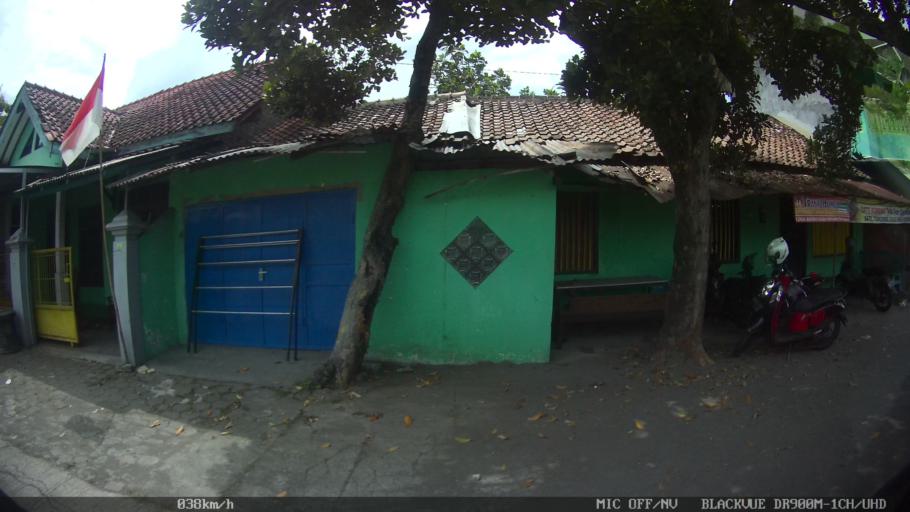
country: ID
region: Daerah Istimewa Yogyakarta
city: Depok
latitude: -7.8129
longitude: 110.4431
